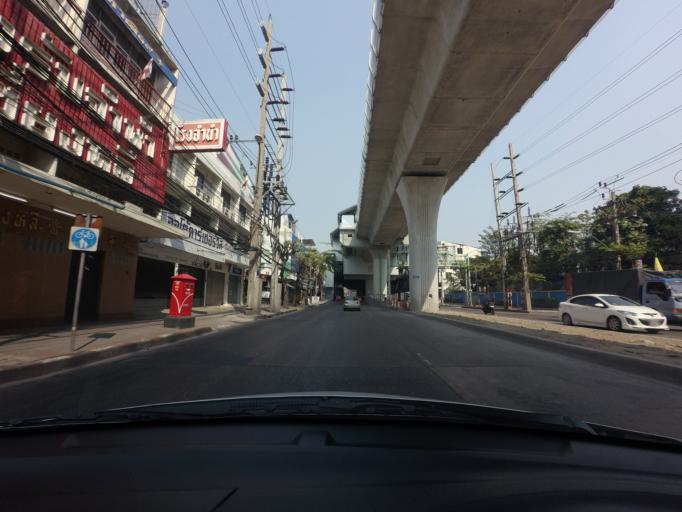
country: TH
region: Bangkok
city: Bangkok Yai
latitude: 13.7390
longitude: 100.4708
